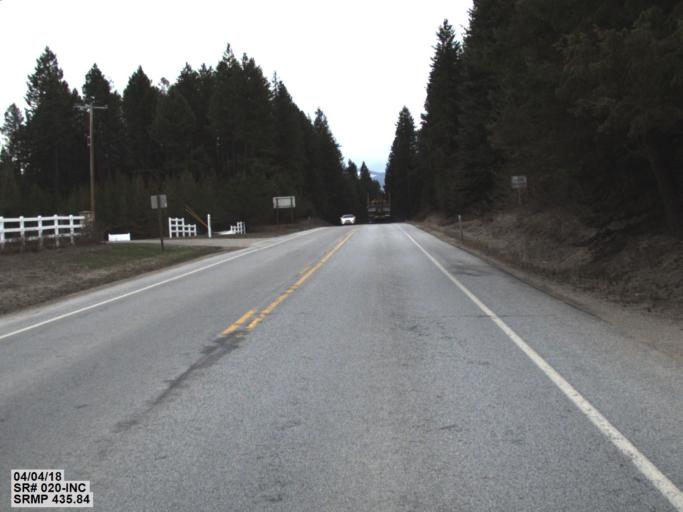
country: US
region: Washington
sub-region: Pend Oreille County
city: Newport
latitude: 48.1960
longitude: -117.0565
